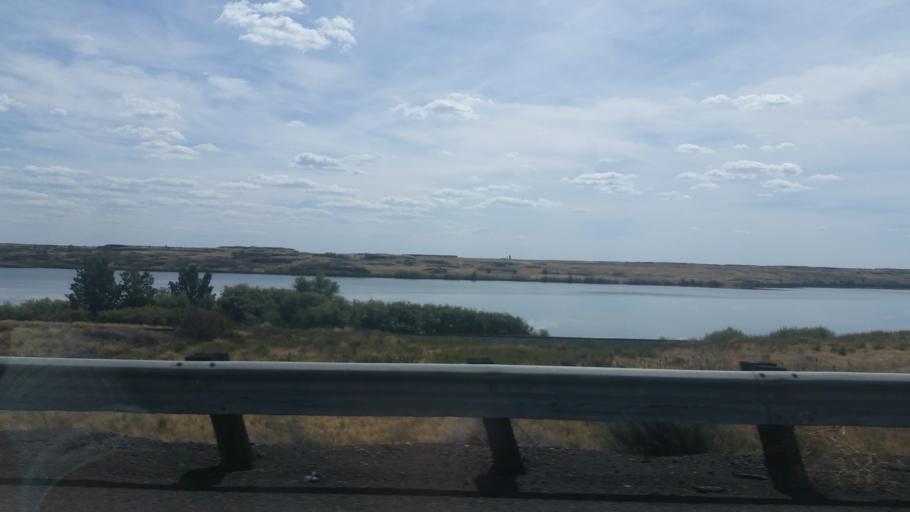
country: US
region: Washington
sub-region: Adams County
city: Ritzville
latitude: 47.2781
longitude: -118.0517
